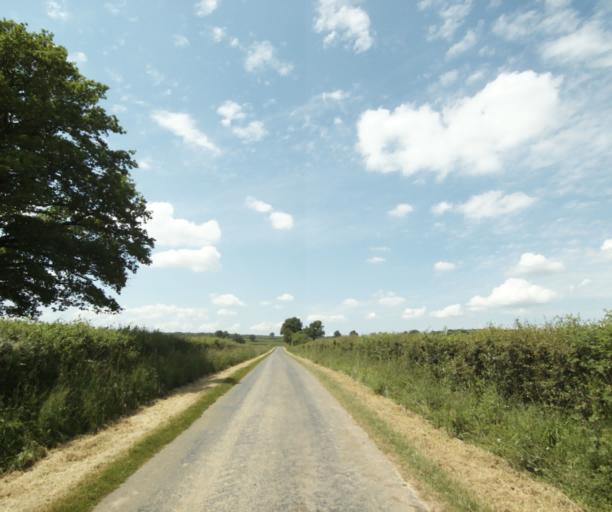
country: FR
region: Bourgogne
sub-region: Departement de Saone-et-Loire
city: Perrecy-les-Forges
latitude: 46.5826
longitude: 4.1459
